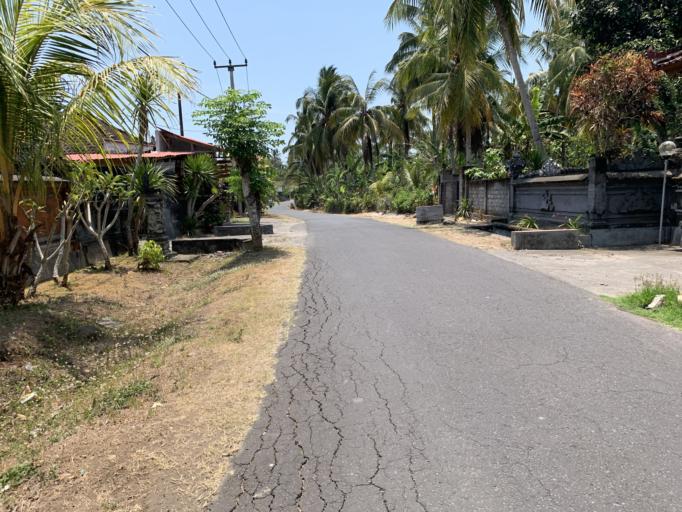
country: ID
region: Bali
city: Banjar Dangin Pangkung
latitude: -8.4314
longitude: 114.8277
